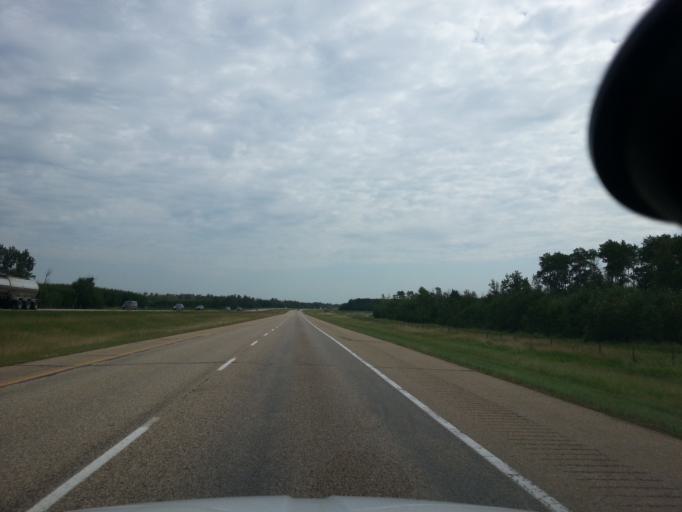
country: CA
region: Alberta
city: Lamont
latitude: 53.5680
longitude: -112.8768
